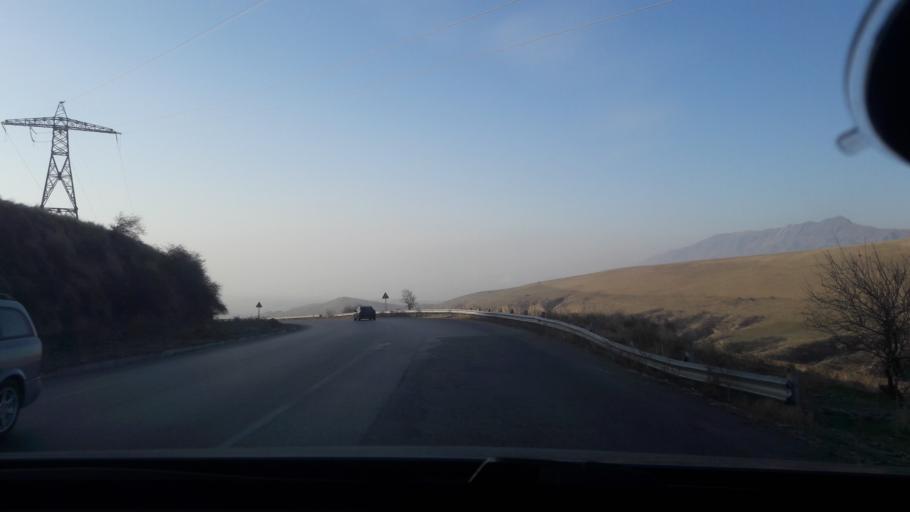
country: TJ
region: Khatlon
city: Danghara
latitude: 38.1969
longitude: 69.2921
